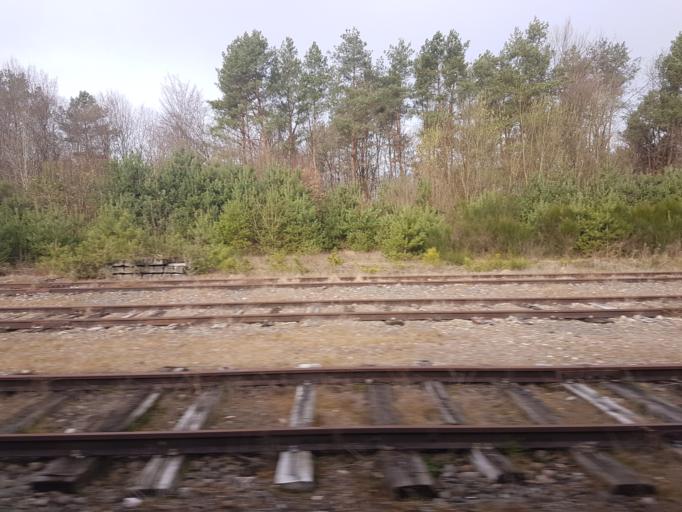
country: FR
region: Franche-Comte
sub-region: Departement de la Haute-Saone
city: Aillevillers-et-Lyaumont
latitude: 47.9122
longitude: 6.3348
